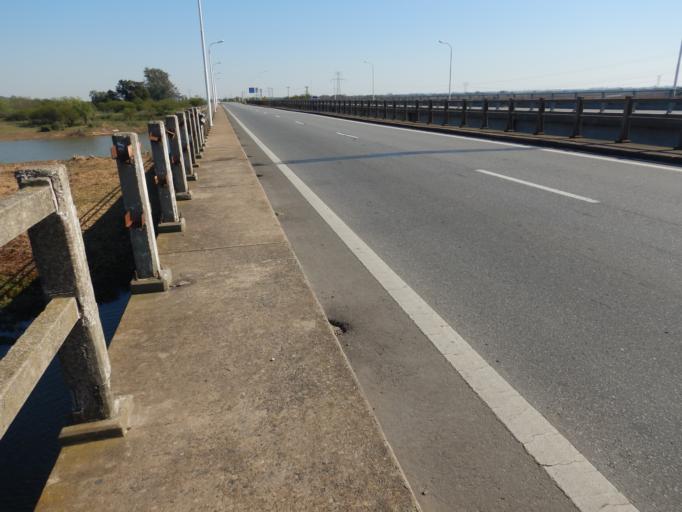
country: AR
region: Entre Rios
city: Parana
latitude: -31.6725
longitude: -60.5784
